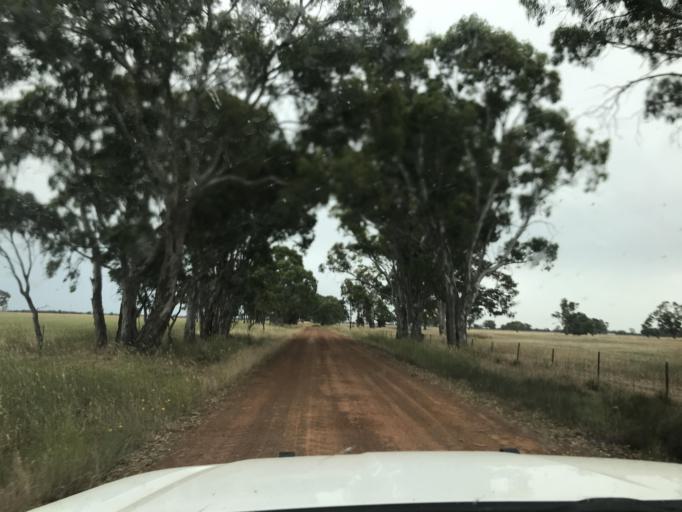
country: AU
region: Victoria
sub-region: Horsham
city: Horsham
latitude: -37.0622
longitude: 141.6281
